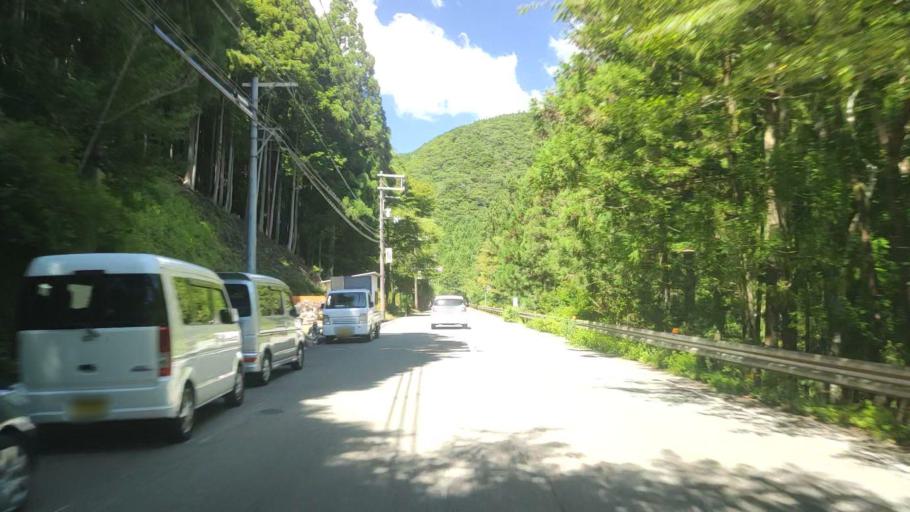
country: JP
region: Mie
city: Owase
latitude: 34.1708
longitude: 136.0016
